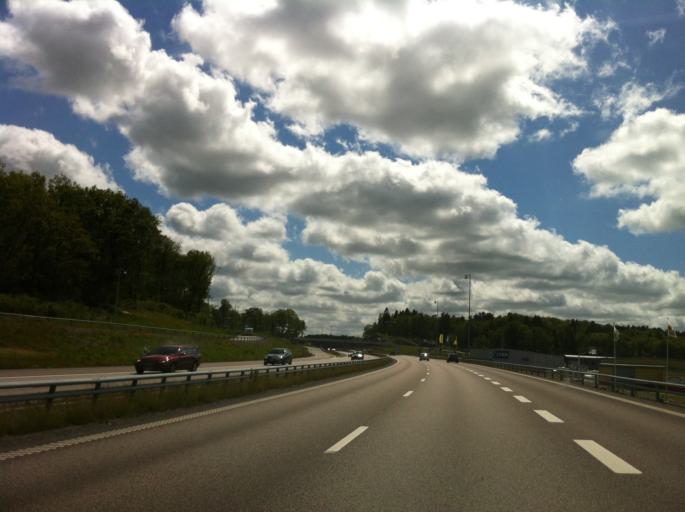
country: SE
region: Vaestra Goetaland
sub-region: Ale Kommun
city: Alvangen
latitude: 57.9551
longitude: 12.1091
